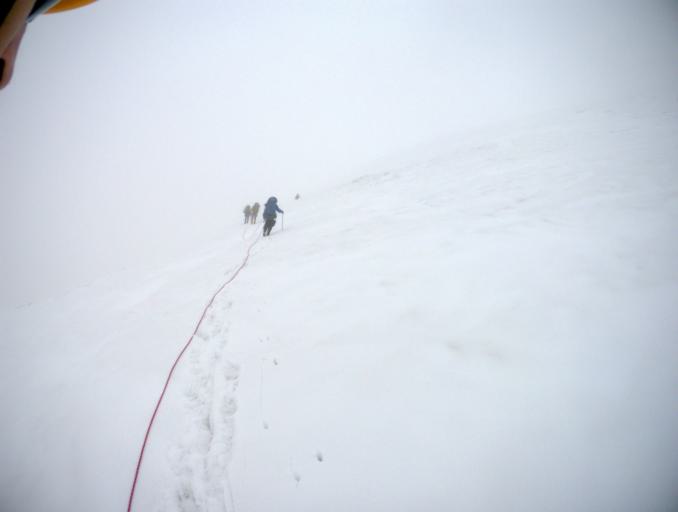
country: RU
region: Kabardino-Balkariya
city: Terskol
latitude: 43.3806
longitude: 42.4660
